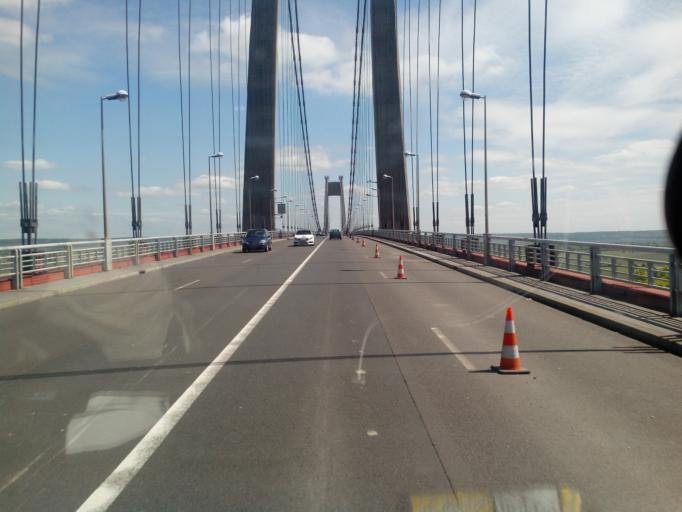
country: FR
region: Haute-Normandie
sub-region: Departement de la Seine-Maritime
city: Tancarville
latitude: 49.4758
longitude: 0.4614
